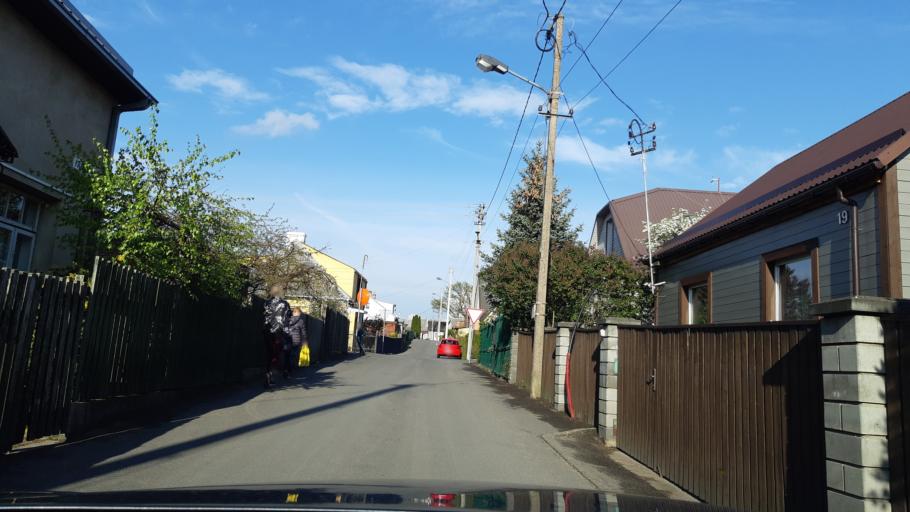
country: LT
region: Kauno apskritis
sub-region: Kaunas
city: Aleksotas
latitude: 54.8668
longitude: 23.9315
